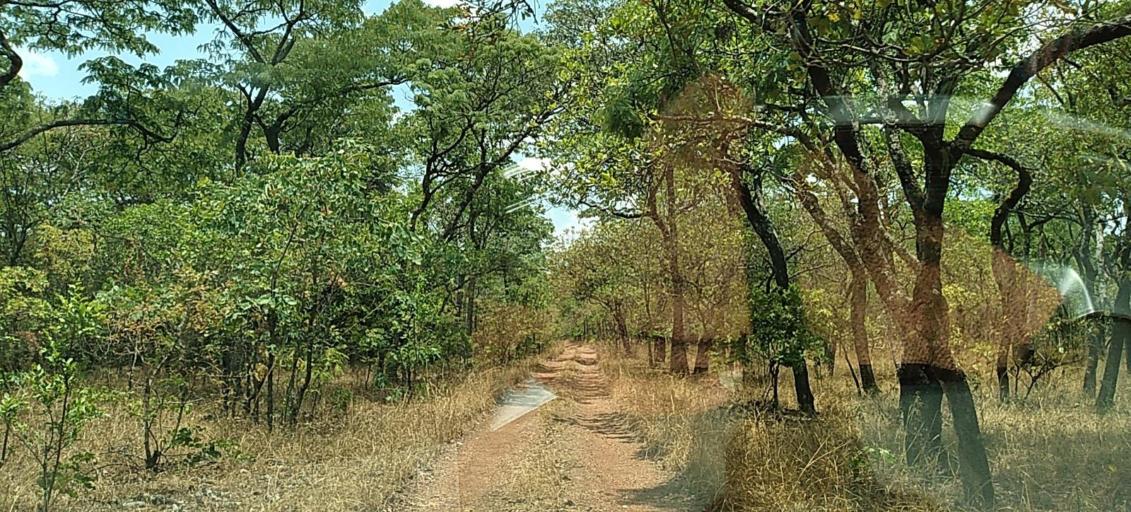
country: ZM
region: Copperbelt
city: Chililabombwe
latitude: -12.4534
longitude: 27.6976
